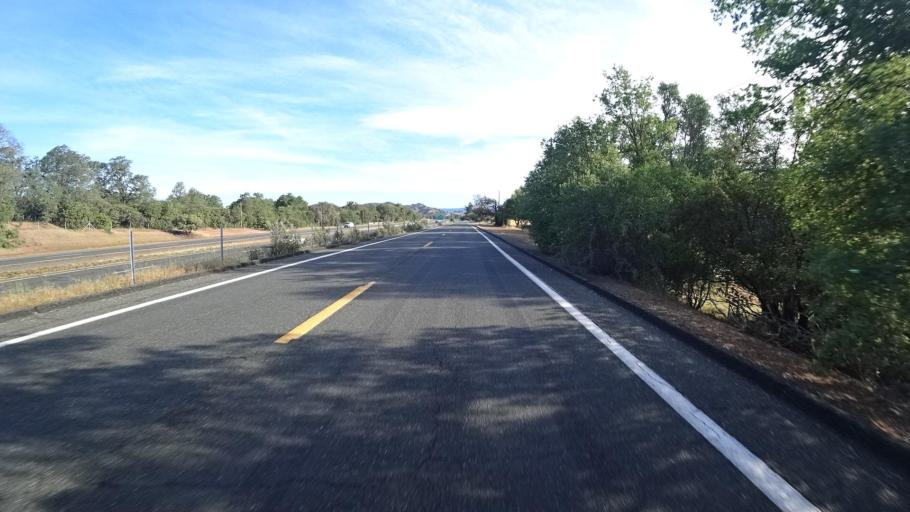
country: US
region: California
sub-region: Lake County
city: Lakeport
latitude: 39.0695
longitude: -122.9312
